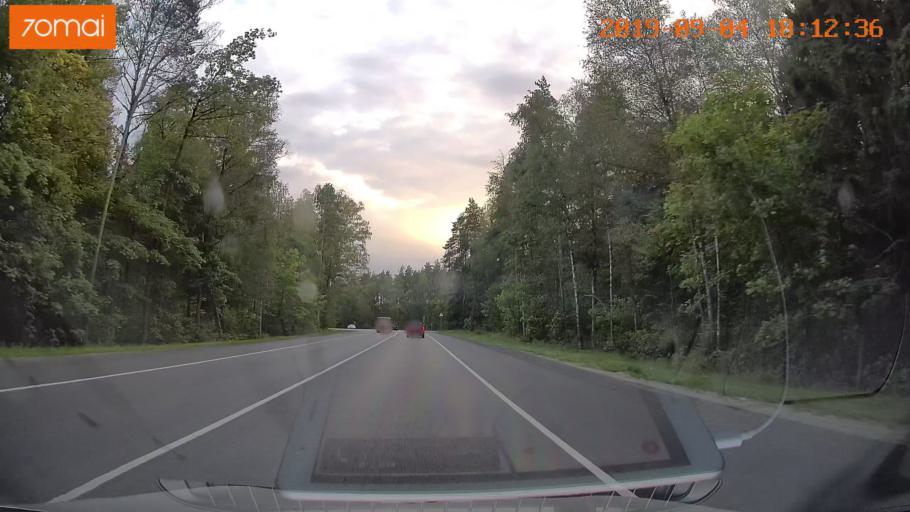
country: RU
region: Moskovskaya
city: Lopatinskiy
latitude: 55.3691
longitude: 38.7393
